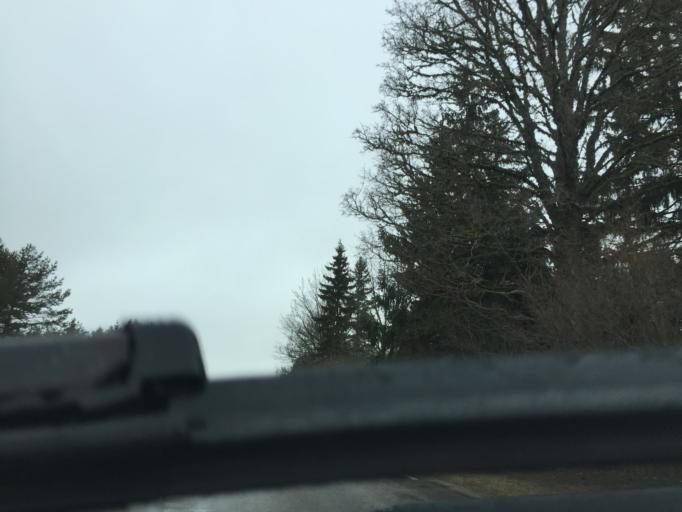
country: EE
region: Laeaene
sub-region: Ridala Parish
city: Uuemoisa
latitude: 58.8743
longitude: 23.6133
